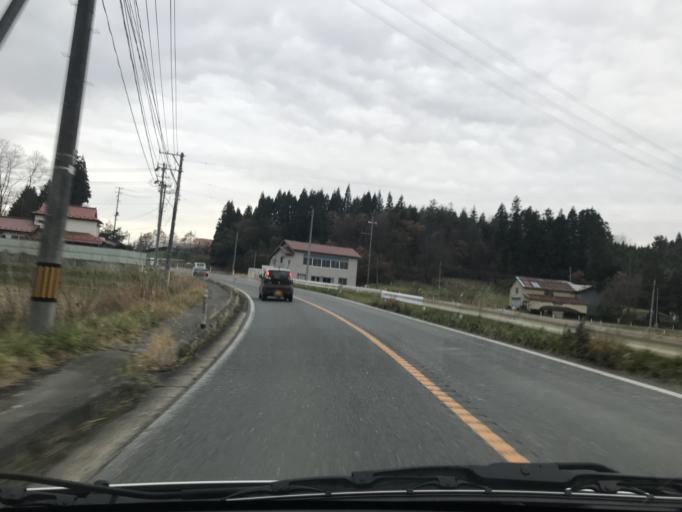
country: JP
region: Iwate
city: Ichinoseki
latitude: 39.0088
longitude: 141.3256
